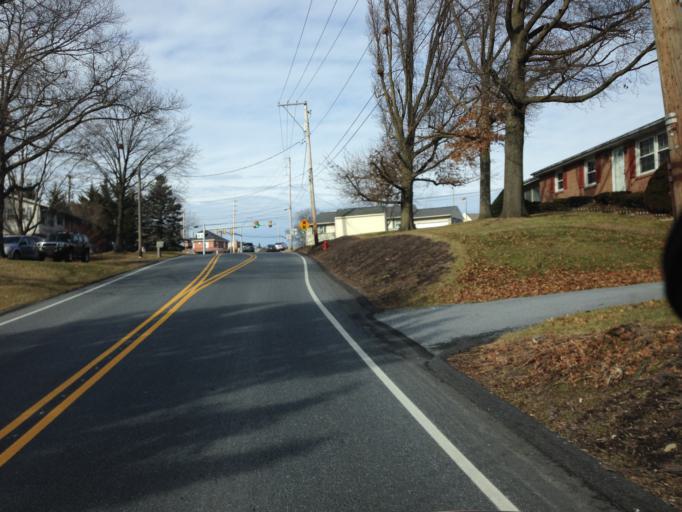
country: US
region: Pennsylvania
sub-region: Lancaster County
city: Manheim
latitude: 40.1721
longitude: -76.3761
